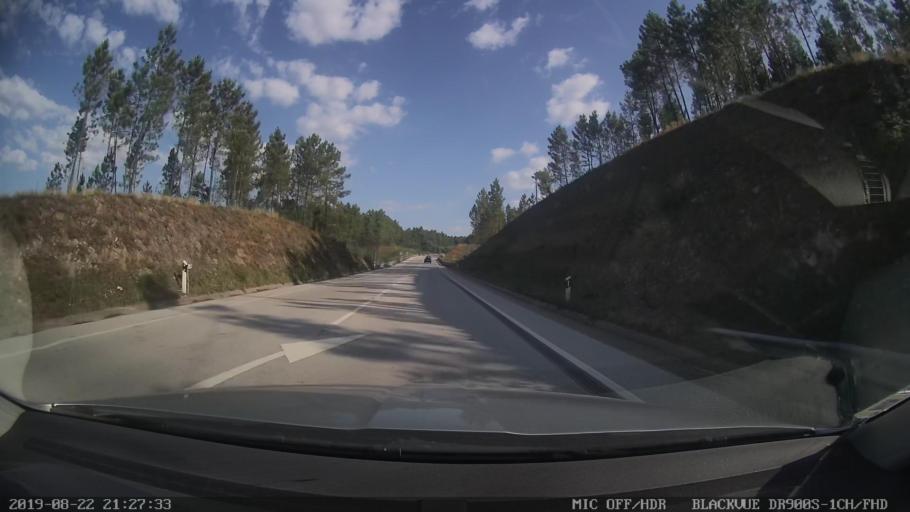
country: PT
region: Leiria
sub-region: Pedrogao Grande
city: Pedrogao Grande
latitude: 39.8799
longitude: -8.1191
